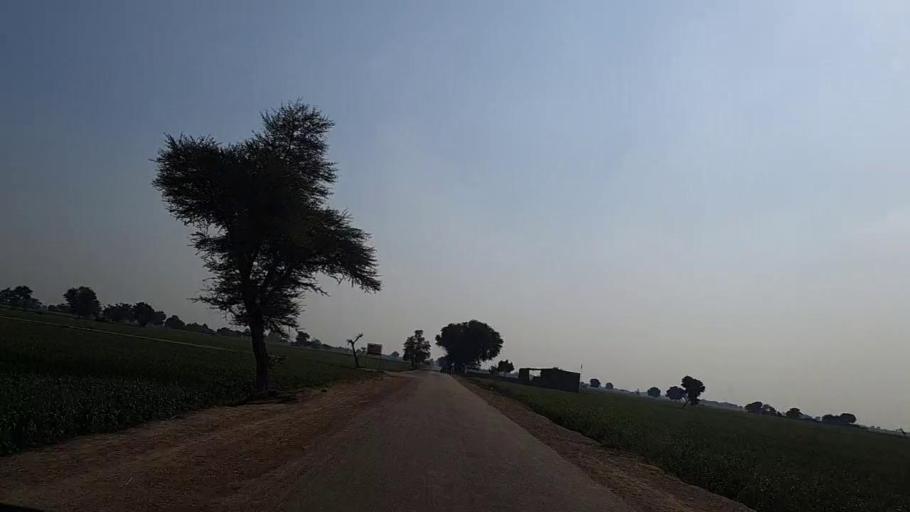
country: PK
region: Sindh
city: Sakrand
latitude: 26.0926
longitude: 68.2904
